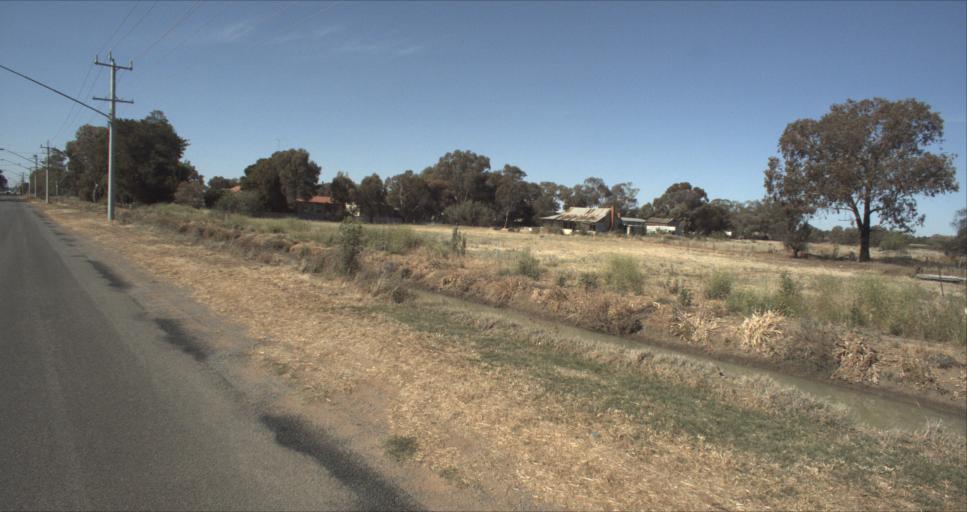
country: AU
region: New South Wales
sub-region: Leeton
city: Leeton
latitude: -34.5686
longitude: 146.4139
